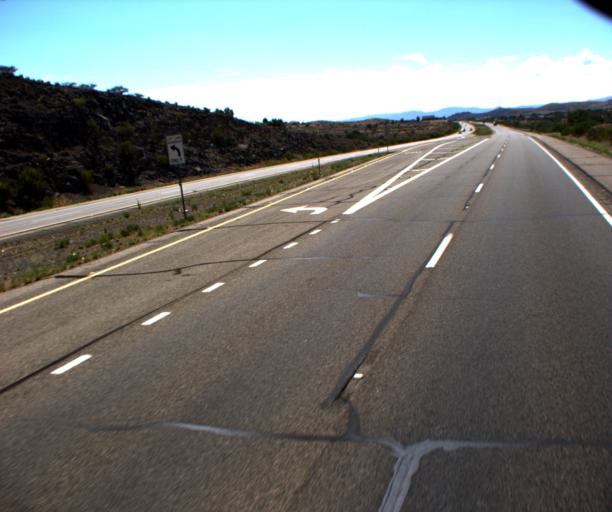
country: US
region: Arizona
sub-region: Yavapai County
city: Spring Valley
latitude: 34.3648
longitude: -112.1768
